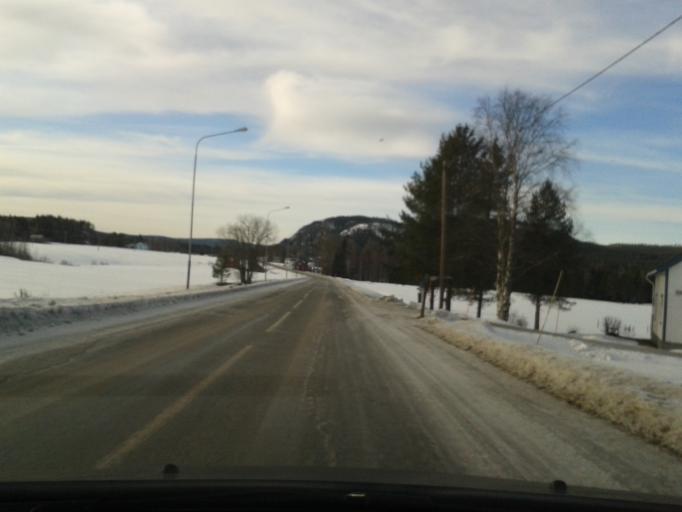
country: SE
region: Vaesternorrland
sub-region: OErnskoeldsviks Kommun
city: Bredbyn
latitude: 63.5256
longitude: 18.0454
